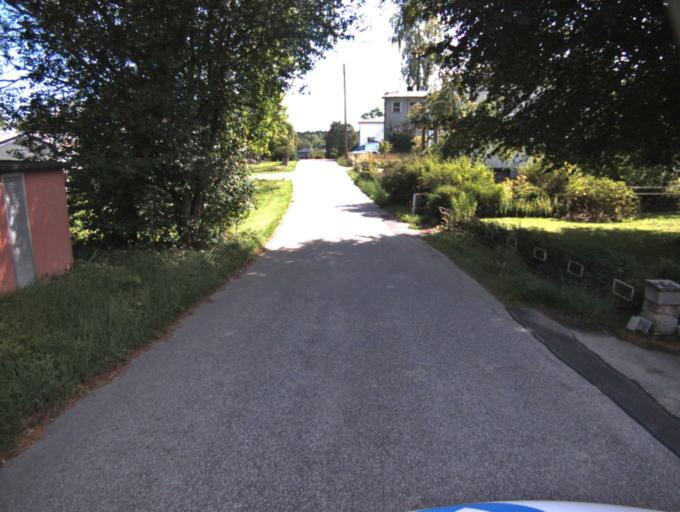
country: SE
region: Vaestra Goetaland
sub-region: Ulricehamns Kommun
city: Ulricehamn
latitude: 57.9006
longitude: 13.4670
